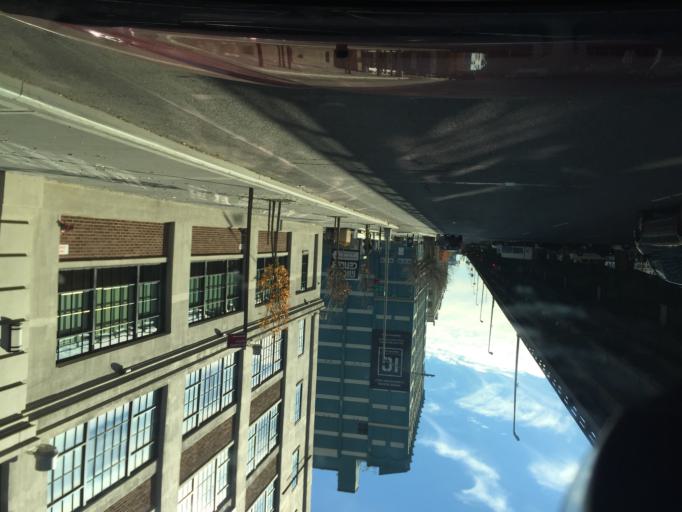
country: US
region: New York
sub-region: Kings County
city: Brooklyn
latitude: 40.6587
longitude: -74.0033
